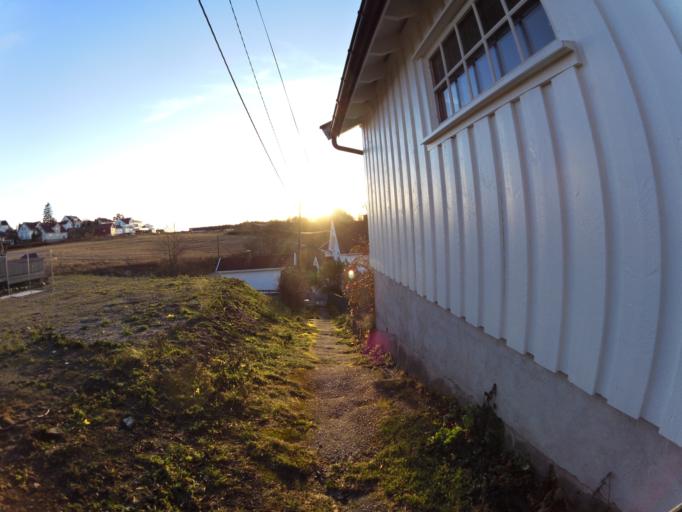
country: NO
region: Ostfold
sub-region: Fredrikstad
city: Fredrikstad
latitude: 59.2471
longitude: 11.0139
